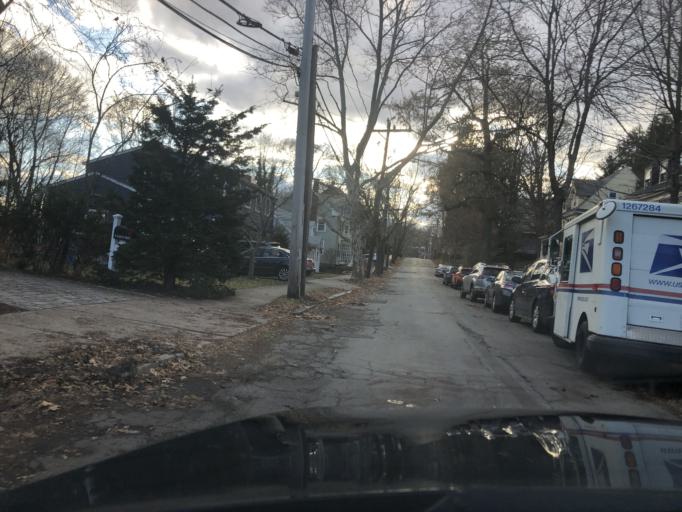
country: US
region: Massachusetts
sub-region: Middlesex County
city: Arlington
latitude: 42.4146
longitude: -71.1577
